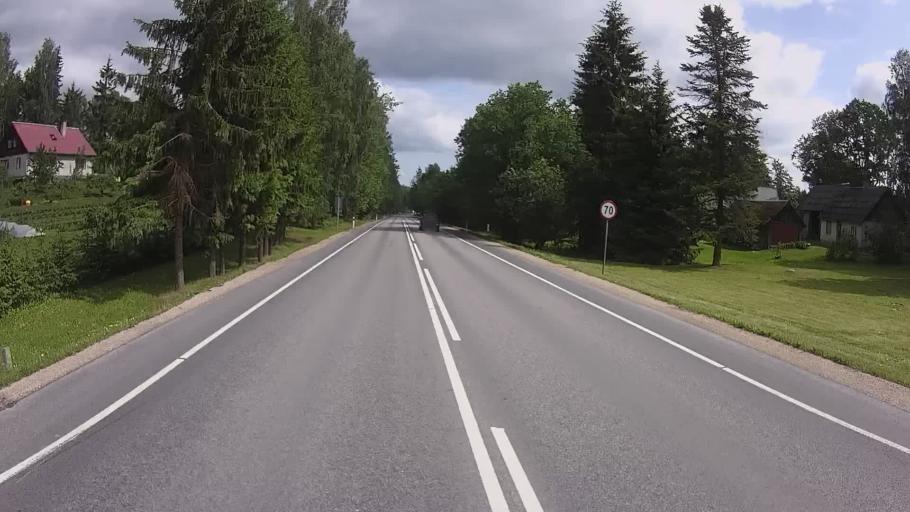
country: EE
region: Polvamaa
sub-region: Polva linn
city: Polva
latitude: 58.0631
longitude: 27.0542
